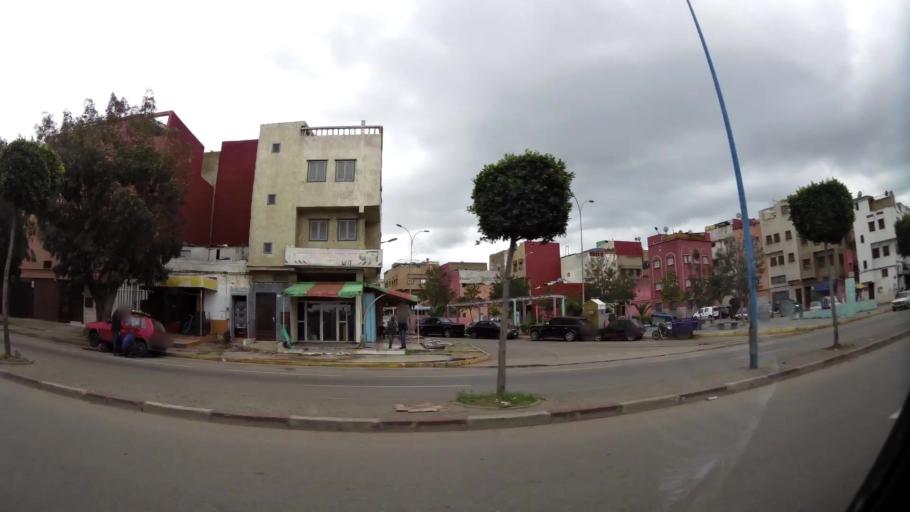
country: MA
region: Grand Casablanca
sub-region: Casablanca
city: Casablanca
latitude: 33.5575
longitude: -7.5577
